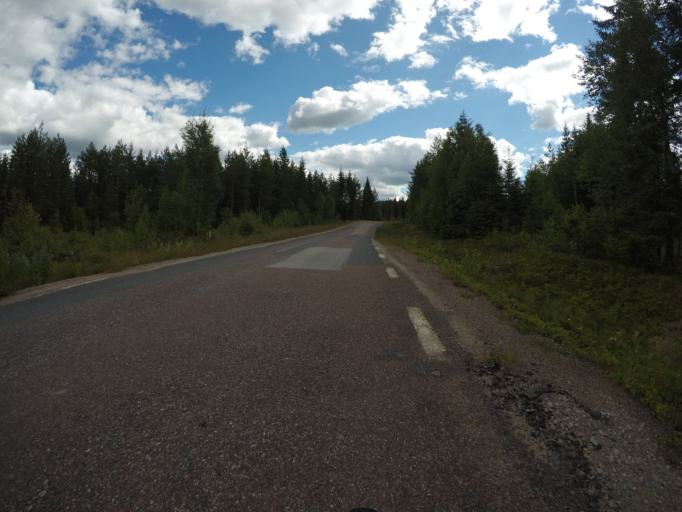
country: SE
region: OErebro
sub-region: Hallefors Kommun
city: Haellefors
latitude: 60.0736
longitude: 14.4897
